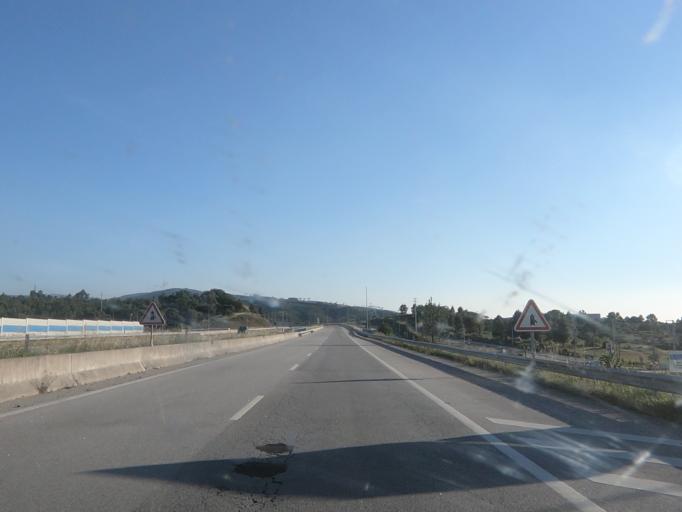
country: PT
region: Guarda
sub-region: Celorico da Beira
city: Celorico da Beira
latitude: 40.6369
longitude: -7.3500
